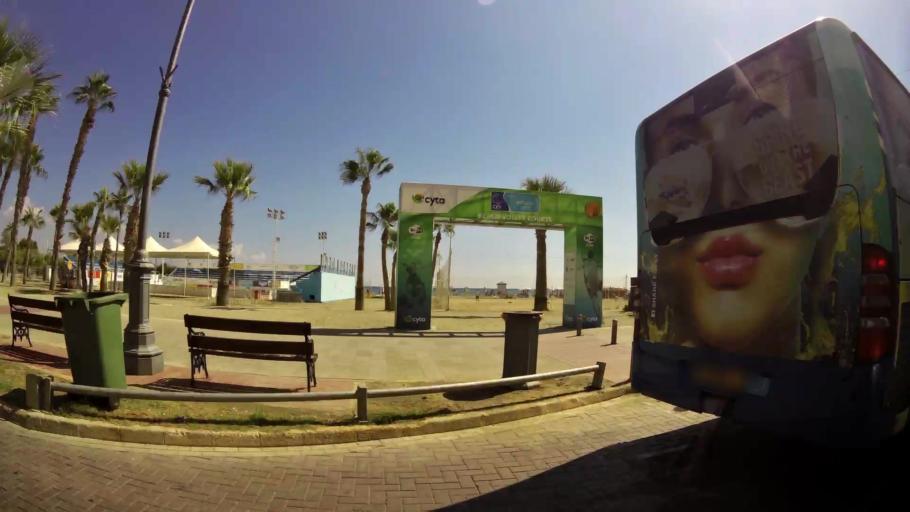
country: CY
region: Larnaka
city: Larnaca
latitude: 34.9156
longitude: 33.6381
